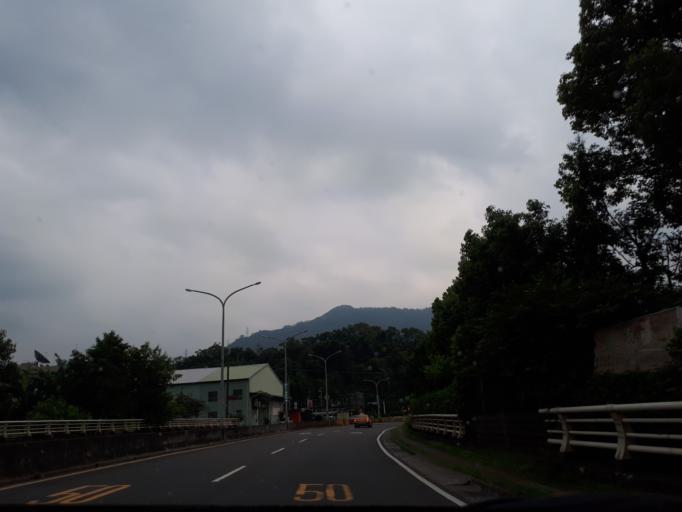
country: TW
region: Taipei
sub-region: Taipei
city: Banqiao
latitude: 24.9594
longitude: 121.5046
